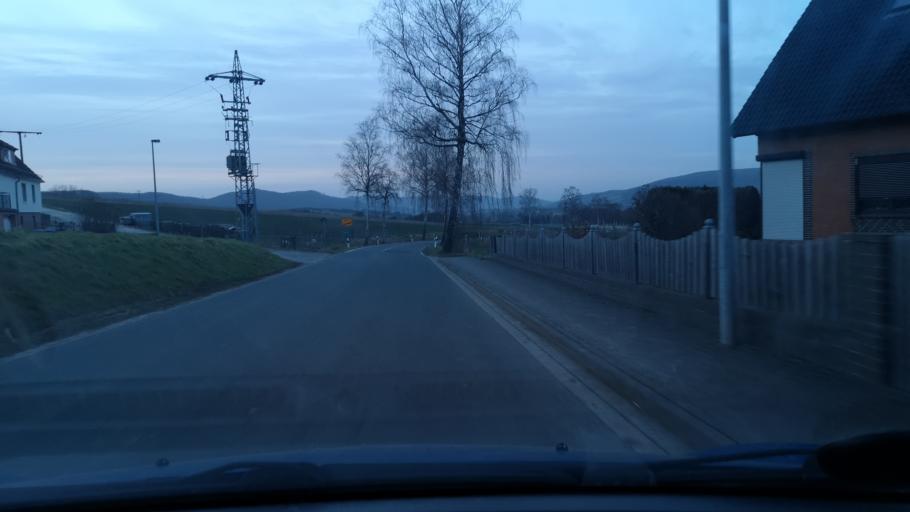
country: DE
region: Lower Saxony
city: Weenzen
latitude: 51.9921
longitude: 9.6499
